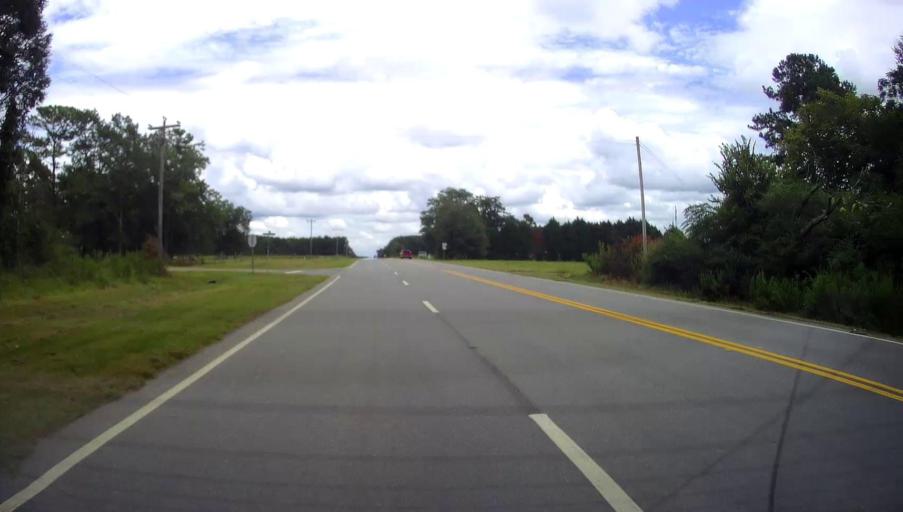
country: US
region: Georgia
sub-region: Schley County
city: Ellaville
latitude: 32.2602
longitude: -84.2162
